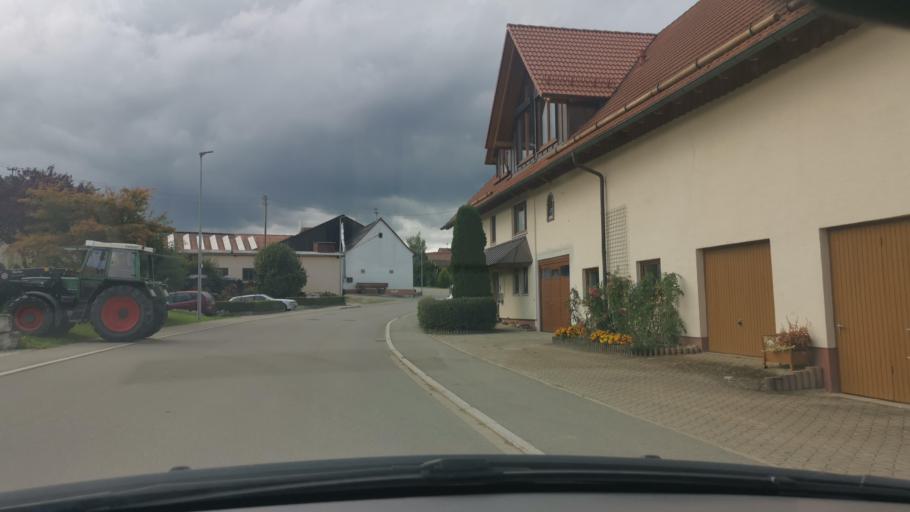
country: DE
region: Baden-Wuerttemberg
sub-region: Tuebingen Region
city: Lauterach
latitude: 48.3092
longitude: 9.6178
